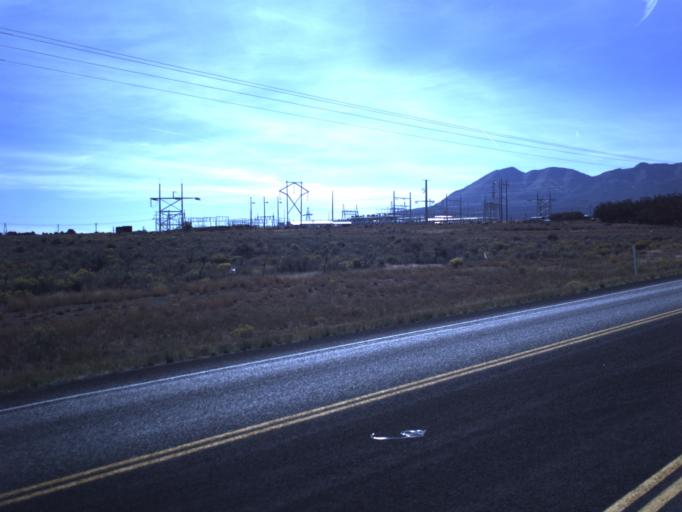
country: US
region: Utah
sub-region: San Juan County
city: Monticello
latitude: 37.8728
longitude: -109.3087
